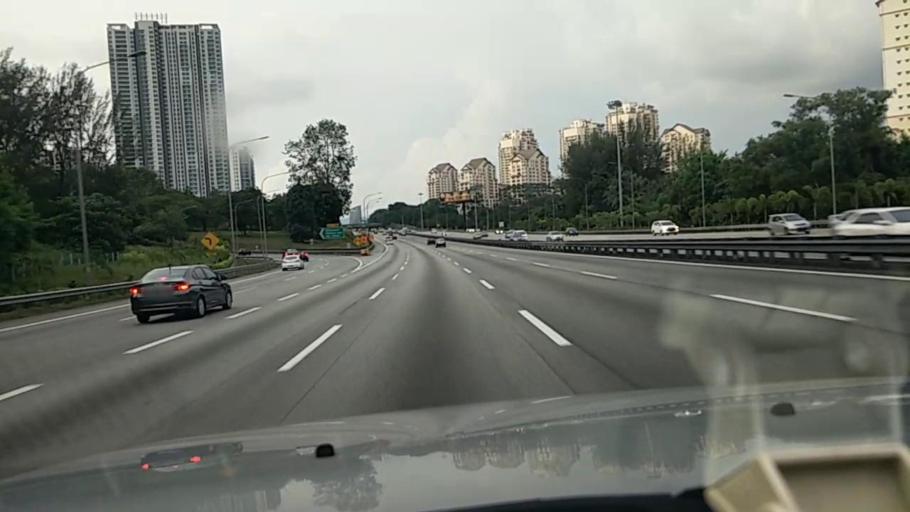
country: MY
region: Selangor
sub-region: Petaling
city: Petaling Jaya
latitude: 3.1306
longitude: 101.5963
